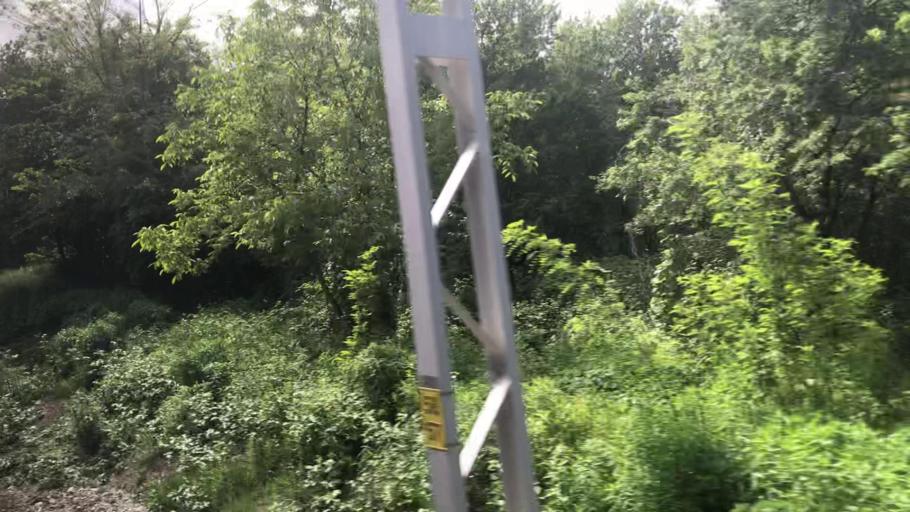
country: PL
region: Lower Silesian Voivodeship
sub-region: Powiat swidnicki
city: Swiebodzice
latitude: 50.8555
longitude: 16.3432
